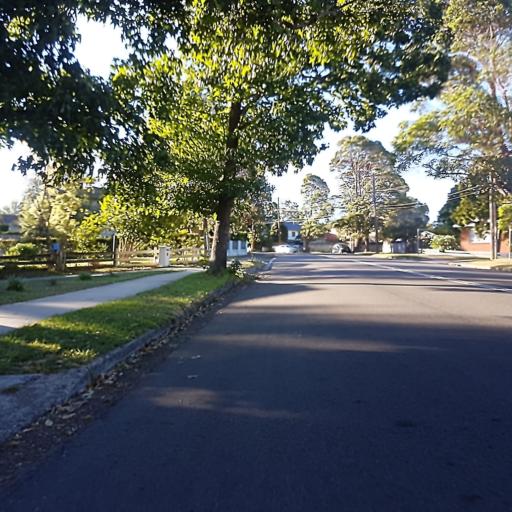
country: AU
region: New South Wales
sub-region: Warringah
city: Davidson
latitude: -33.7427
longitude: 151.2181
